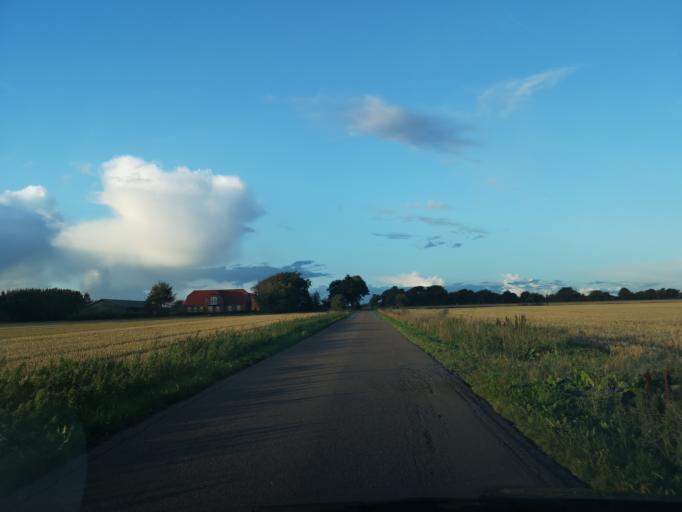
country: DK
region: Central Jutland
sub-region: Ringkobing-Skjern Kommune
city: Videbaek
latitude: 56.0271
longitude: 8.5636
